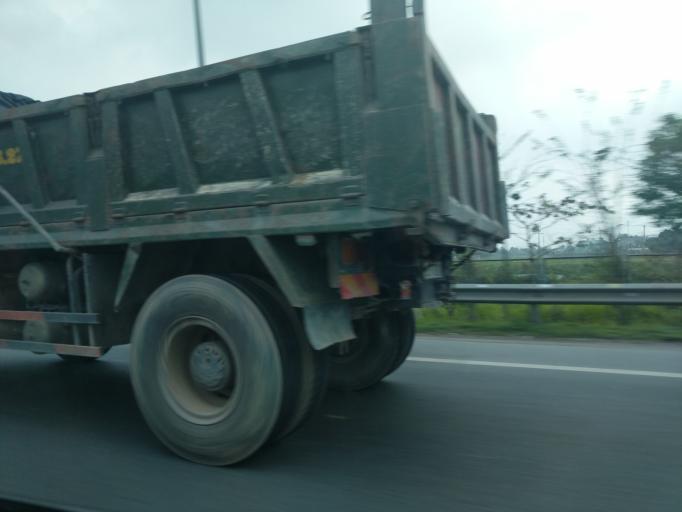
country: VN
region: Ha Noi
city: Dong Anh
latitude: 21.1580
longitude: 105.8195
